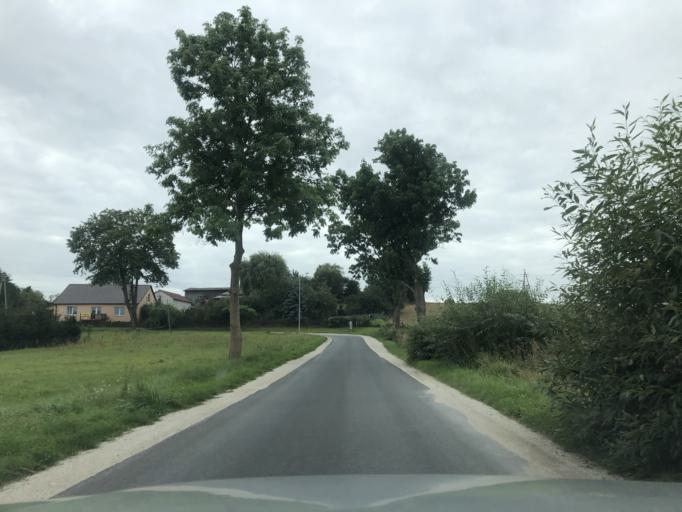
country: PL
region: Greater Poland Voivodeship
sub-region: Powiat pilski
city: Pila
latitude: 53.2668
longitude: 16.6893
